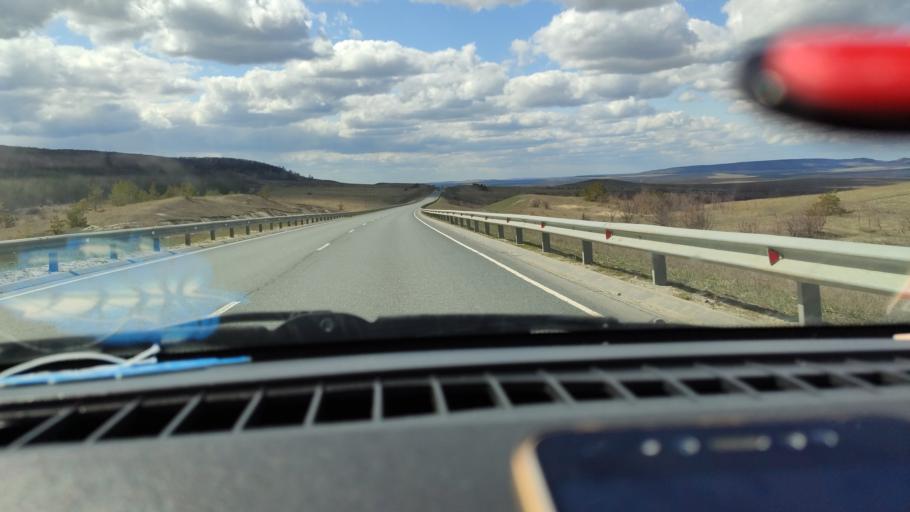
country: RU
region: Saratov
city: Alekseyevka
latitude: 52.3635
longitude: 47.9577
